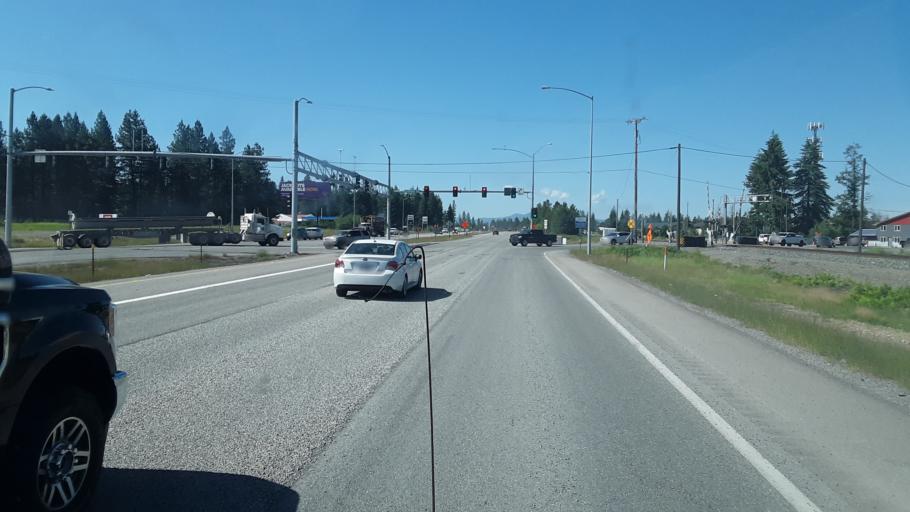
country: US
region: Idaho
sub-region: Kootenai County
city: Hayden
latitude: 47.8326
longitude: -116.7774
